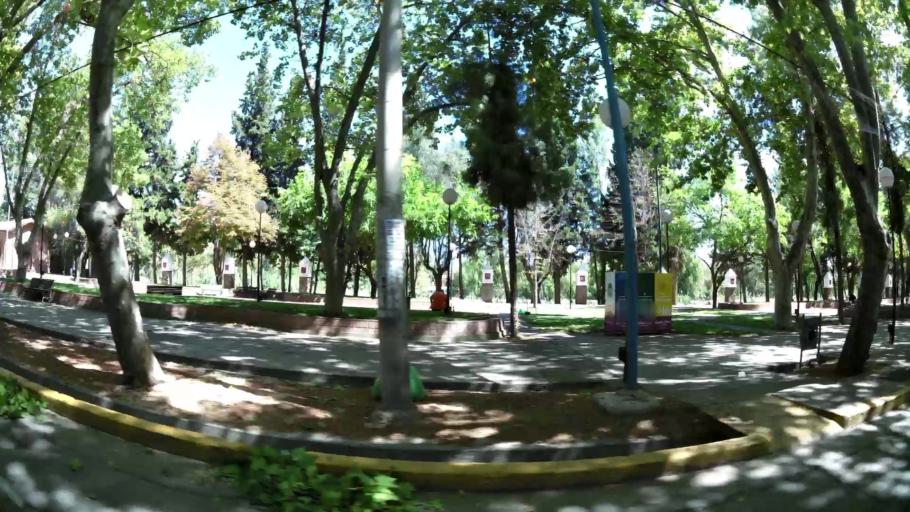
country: AR
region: Mendoza
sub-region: Departamento de Godoy Cruz
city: Godoy Cruz
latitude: -32.9580
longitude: -68.8519
